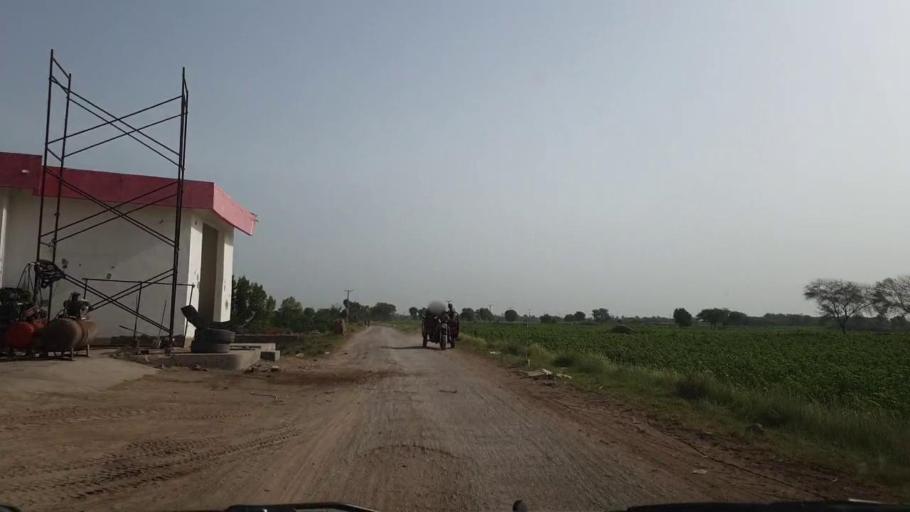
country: PK
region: Sindh
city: Nawabshah
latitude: 26.2193
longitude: 68.4043
